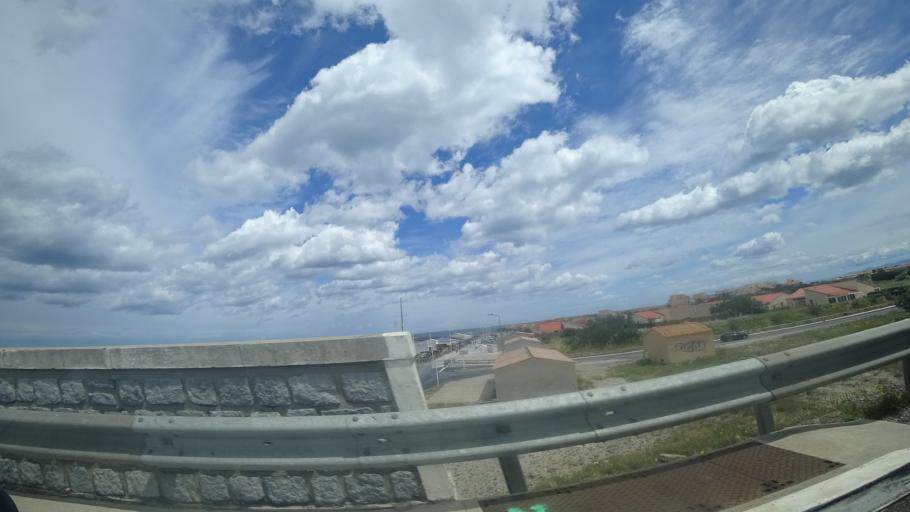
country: FR
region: Languedoc-Roussillon
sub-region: Departement de l'Aude
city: Leucate
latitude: 42.8860
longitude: 3.0477
